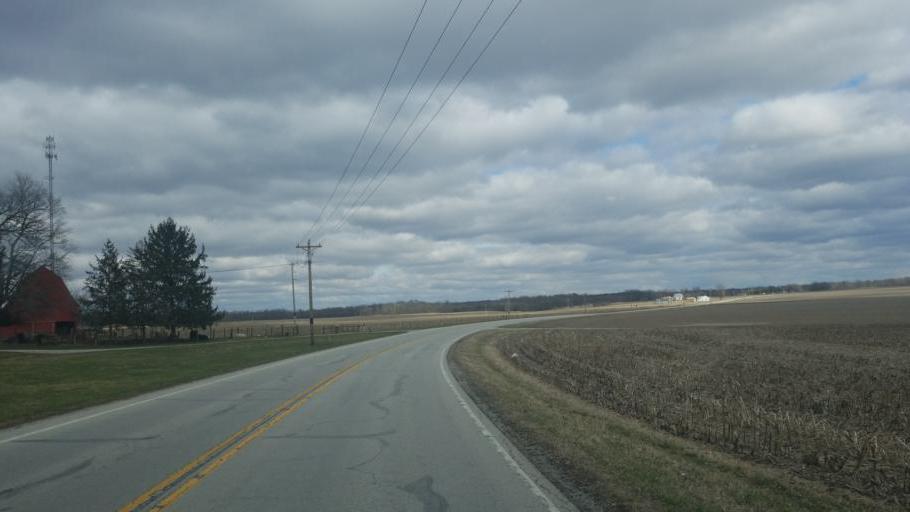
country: US
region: Indiana
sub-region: Putnam County
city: Greencastle
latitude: 39.7619
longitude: -86.9813
